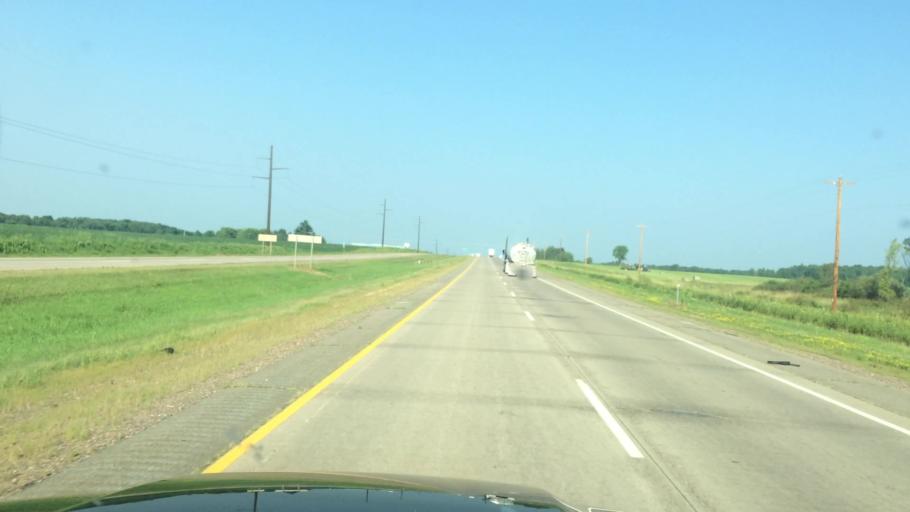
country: US
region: Wisconsin
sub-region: Marathon County
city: Edgar
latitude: 44.9444
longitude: -89.9965
